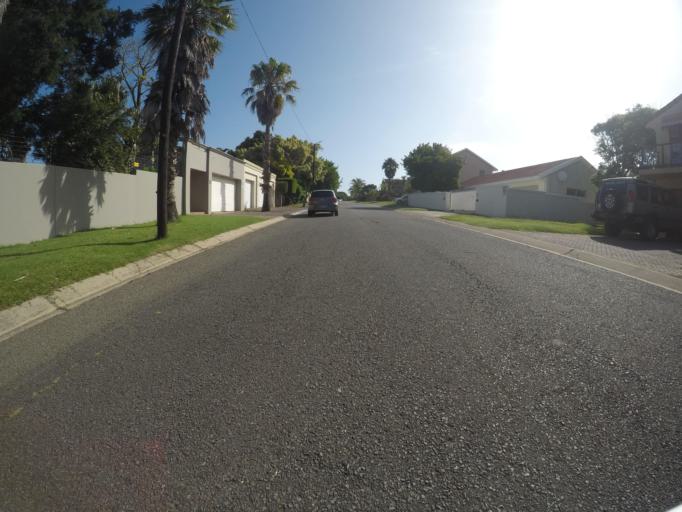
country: ZA
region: Eastern Cape
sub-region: Buffalo City Metropolitan Municipality
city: East London
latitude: -32.9737
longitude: 27.9571
